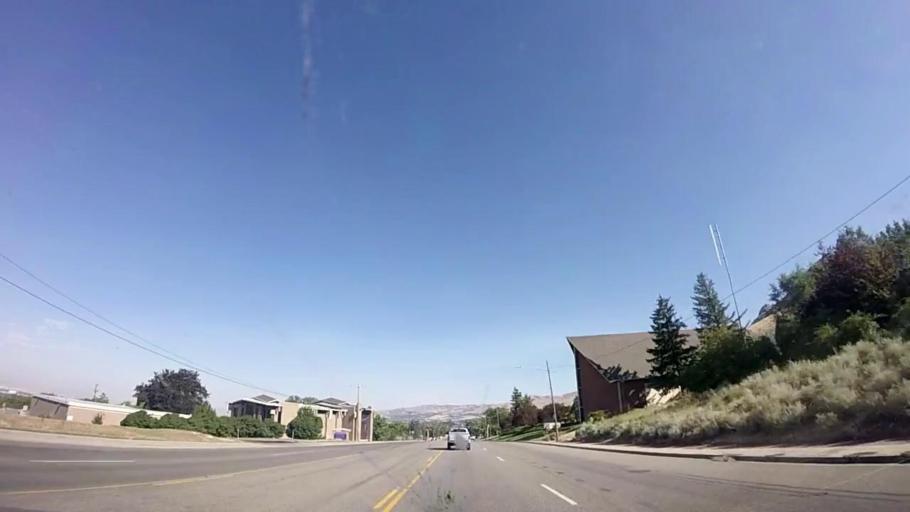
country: US
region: Utah
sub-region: Salt Lake County
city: Canyon Rim
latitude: 40.7239
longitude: -111.8135
